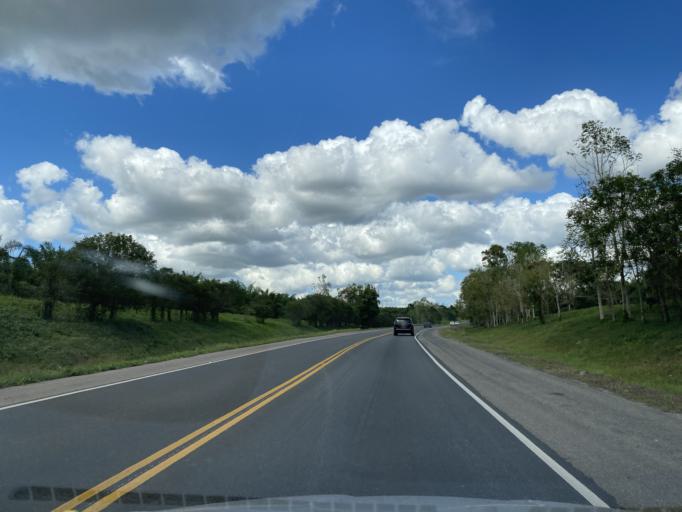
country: DO
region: Monte Plata
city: Monte Plata
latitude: 18.7203
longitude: -69.7601
